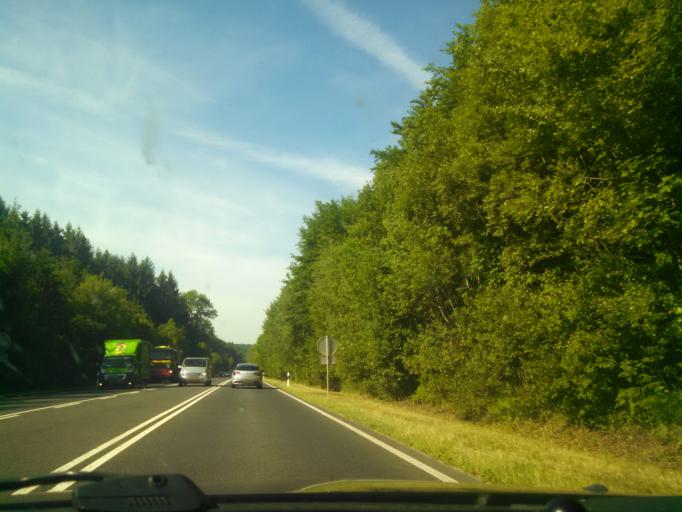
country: LU
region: Grevenmacher
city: Gonderange
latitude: 49.6817
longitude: 6.2227
